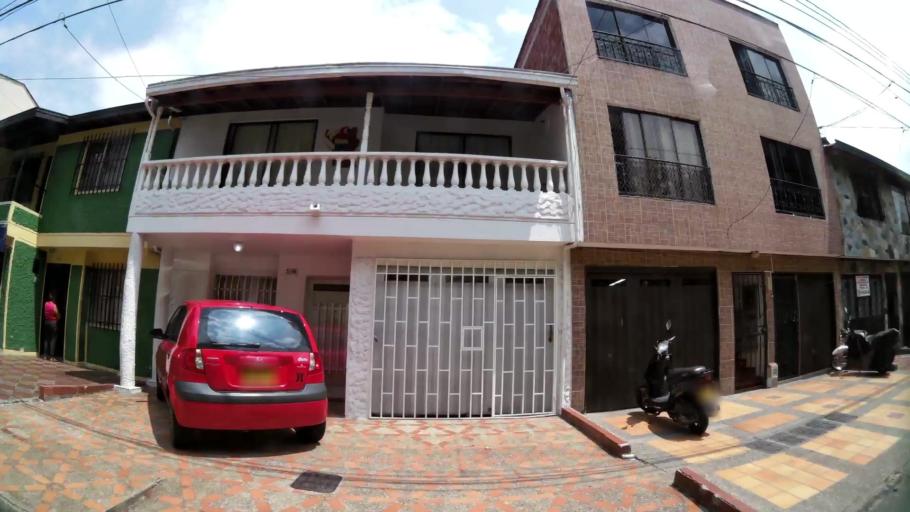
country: CO
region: Antioquia
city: Itagui
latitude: 6.1921
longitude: -75.5946
